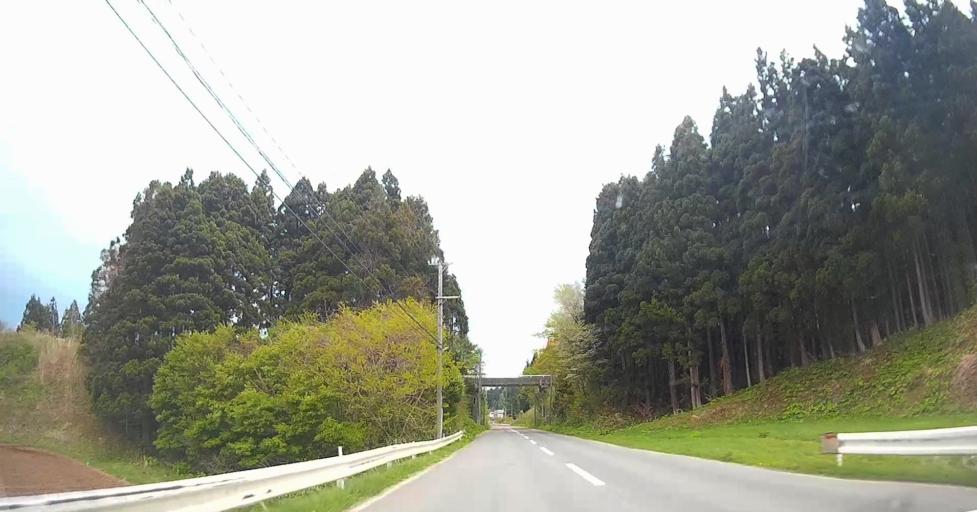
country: JP
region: Aomori
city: Shimokizukuri
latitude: 41.1808
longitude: 140.4607
